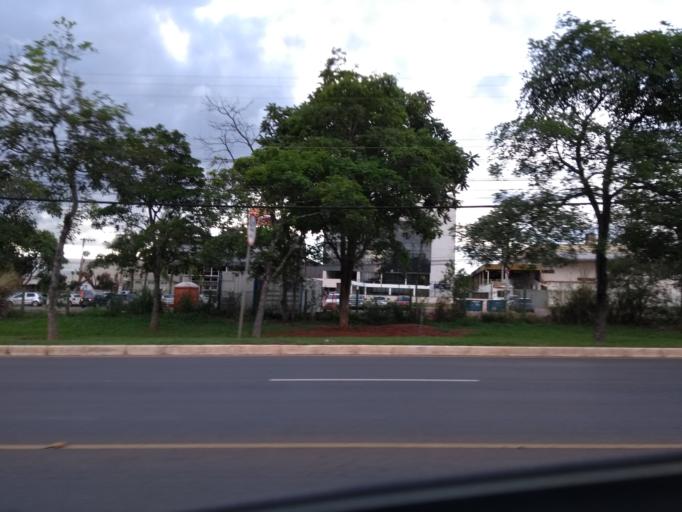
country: BR
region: Federal District
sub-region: Brasilia
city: Brasilia
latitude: -15.7921
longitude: -47.9093
